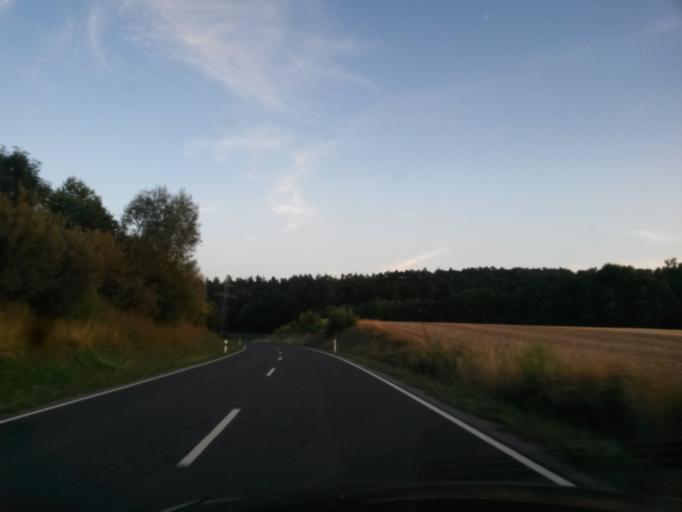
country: DE
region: Bavaria
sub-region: Regierungsbezirk Unterfranken
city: Marktheidenfeld
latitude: 49.8217
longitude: 9.6187
